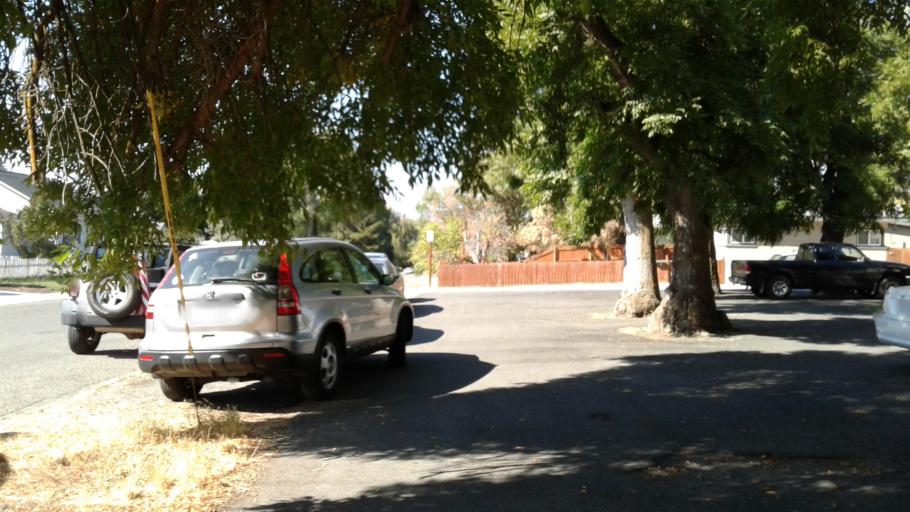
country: US
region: Washington
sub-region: Kittitas County
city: Ellensburg
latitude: 47.0030
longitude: -120.5453
